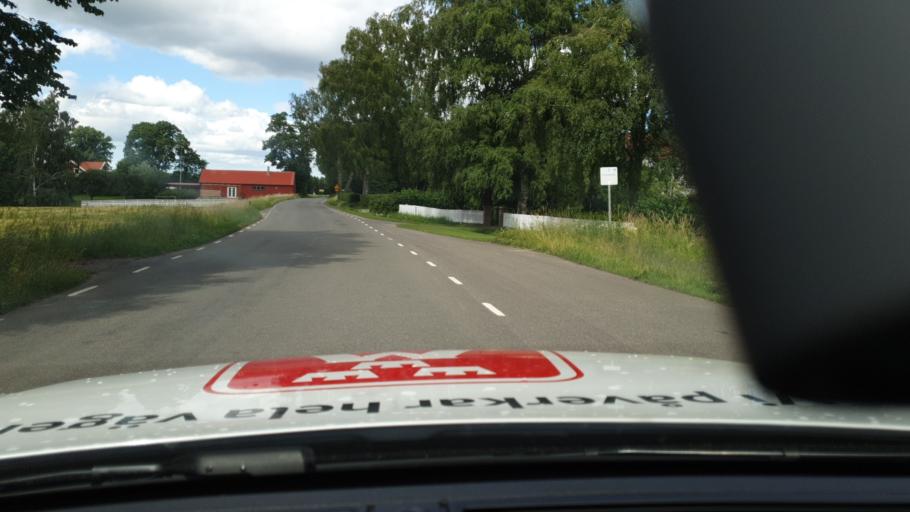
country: SE
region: Vaestra Goetaland
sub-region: Skara Kommun
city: Axvall
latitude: 58.3764
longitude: 13.6420
